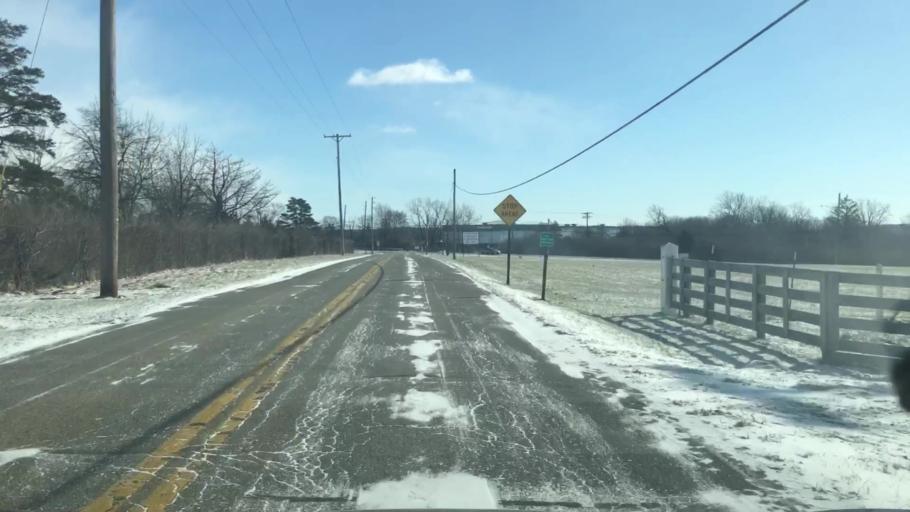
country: US
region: Ohio
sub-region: Greene County
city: Fairborn
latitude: 39.8402
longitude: -84.0064
